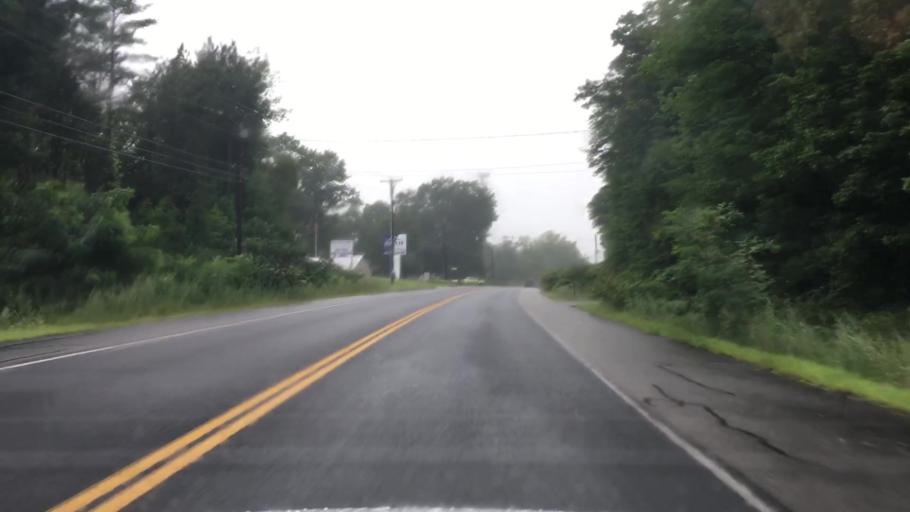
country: US
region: Maine
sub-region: Cumberland County
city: South Windham
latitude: 43.7641
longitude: -70.3745
